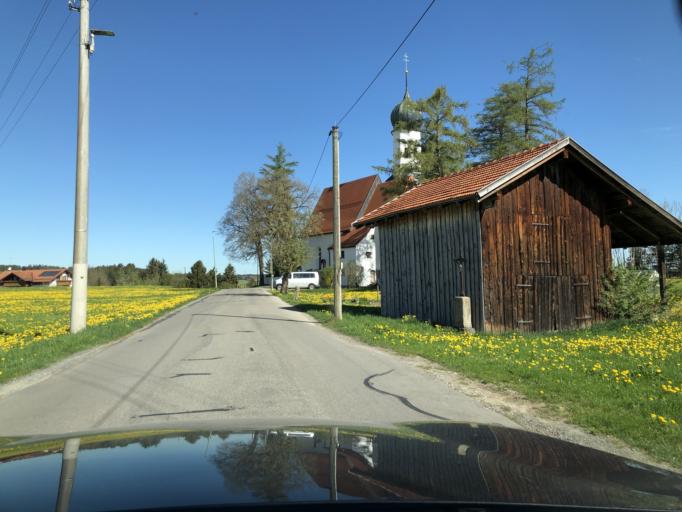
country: DE
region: Bavaria
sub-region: Swabia
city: Wald
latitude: 47.7500
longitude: 10.5731
